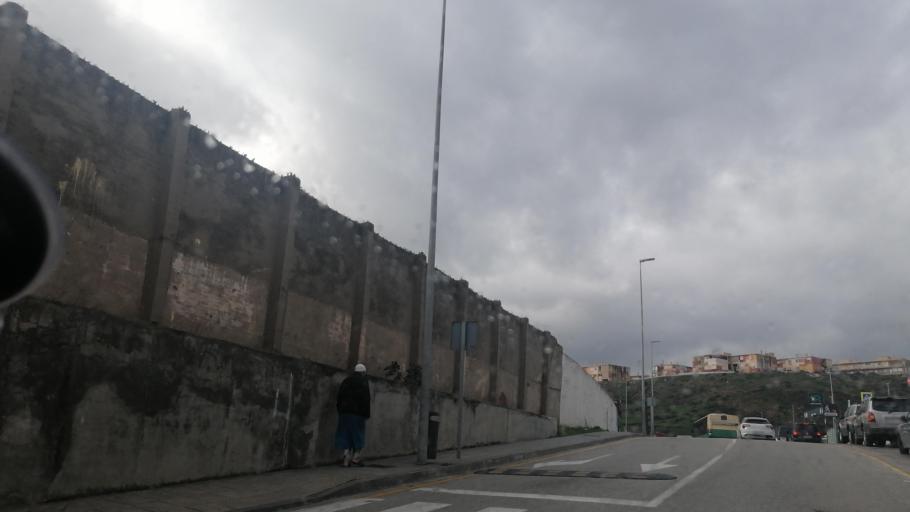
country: ES
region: Ceuta
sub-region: Ceuta
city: Ceuta
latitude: 35.8804
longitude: -5.3352
